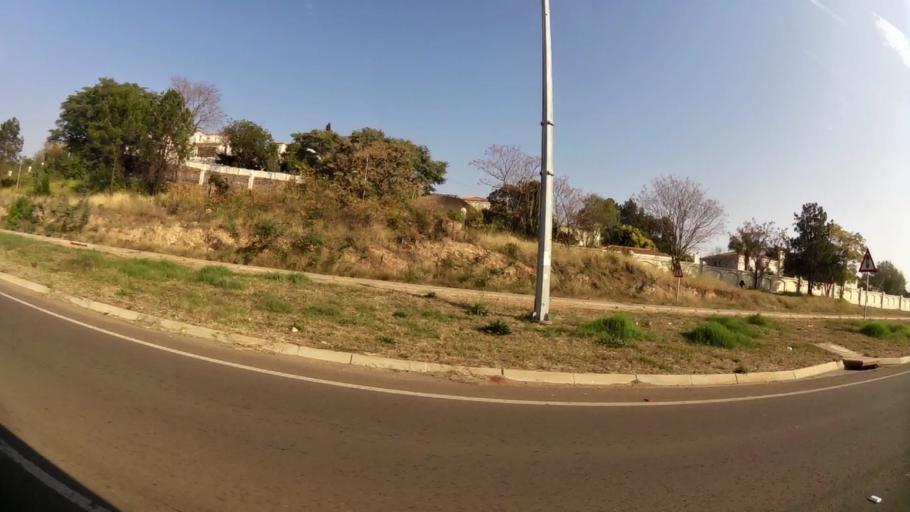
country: ZA
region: Gauteng
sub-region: City of Tshwane Metropolitan Municipality
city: Pretoria
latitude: -25.7463
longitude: 28.3282
